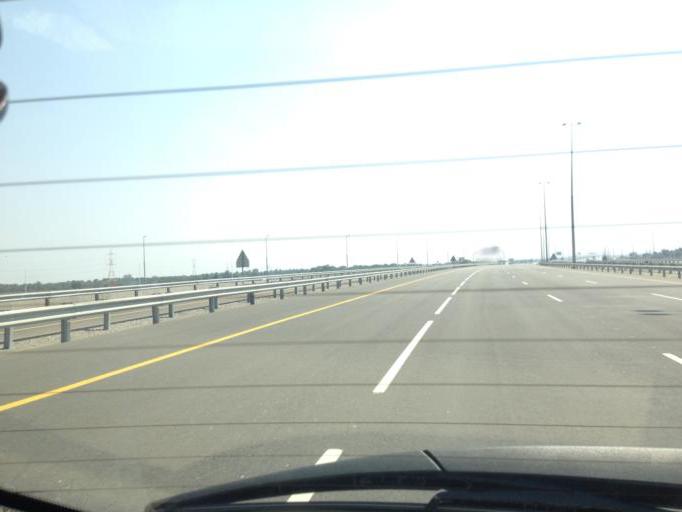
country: OM
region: Al Batinah
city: Barka'
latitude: 23.6325
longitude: 57.8746
